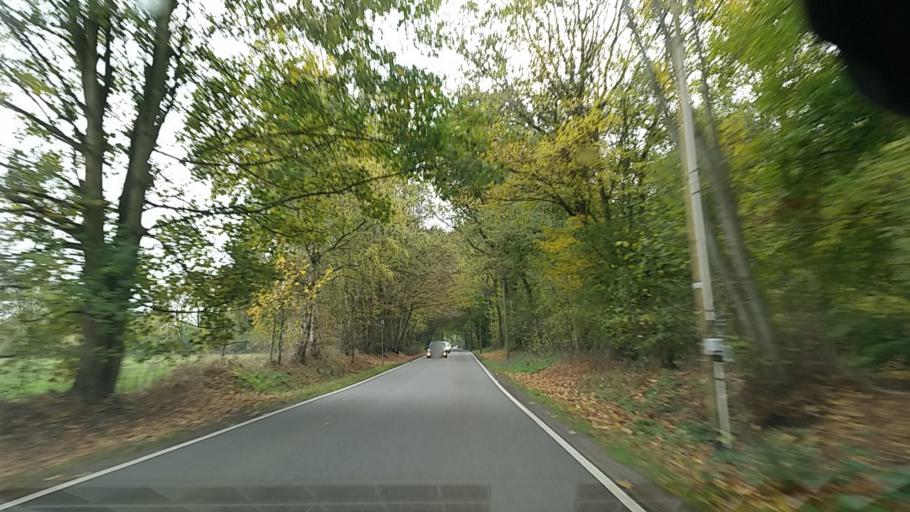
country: DE
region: Schleswig-Holstein
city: Oststeinbek
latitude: 53.5580
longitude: 10.1490
